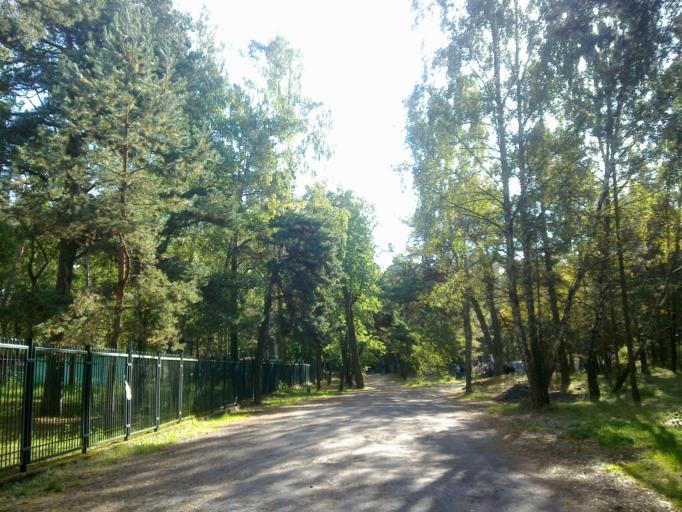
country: PL
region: Pomeranian Voivodeship
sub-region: Gdansk
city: Gdansk
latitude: 54.3708
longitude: 18.7291
